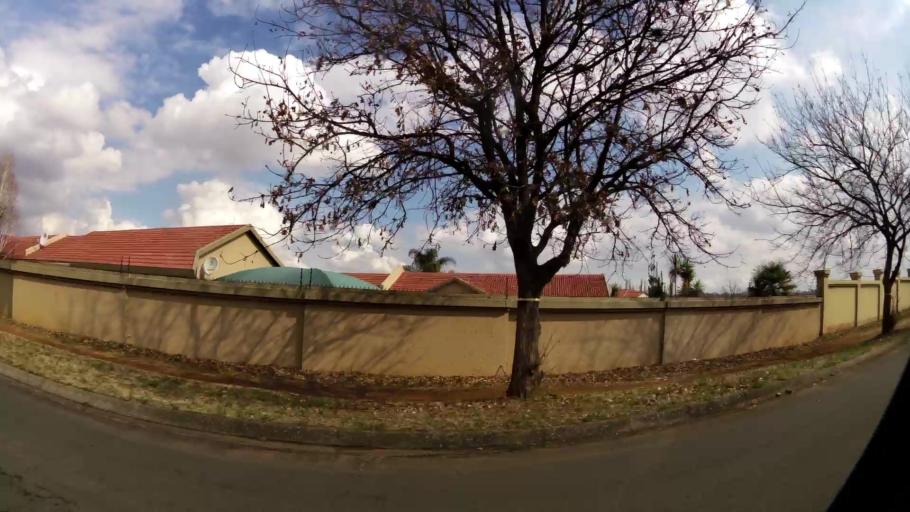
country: ZA
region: Gauteng
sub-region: Sedibeng District Municipality
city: Vanderbijlpark
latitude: -26.7362
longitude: 27.8432
